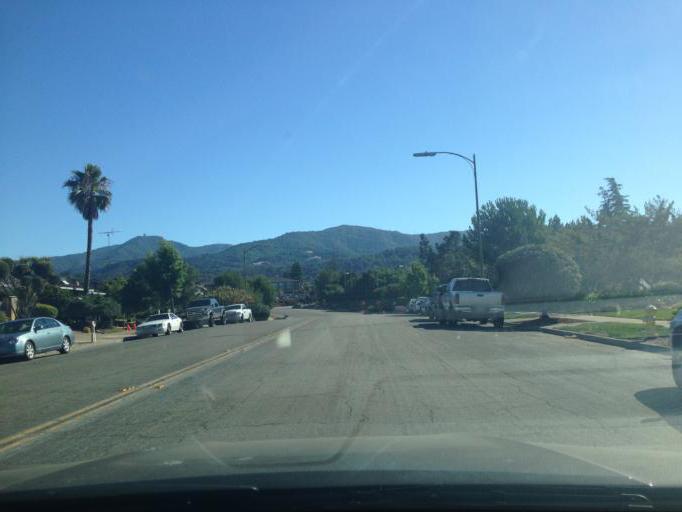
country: US
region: California
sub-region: Santa Clara County
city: Seven Trees
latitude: 37.2165
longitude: -121.8643
